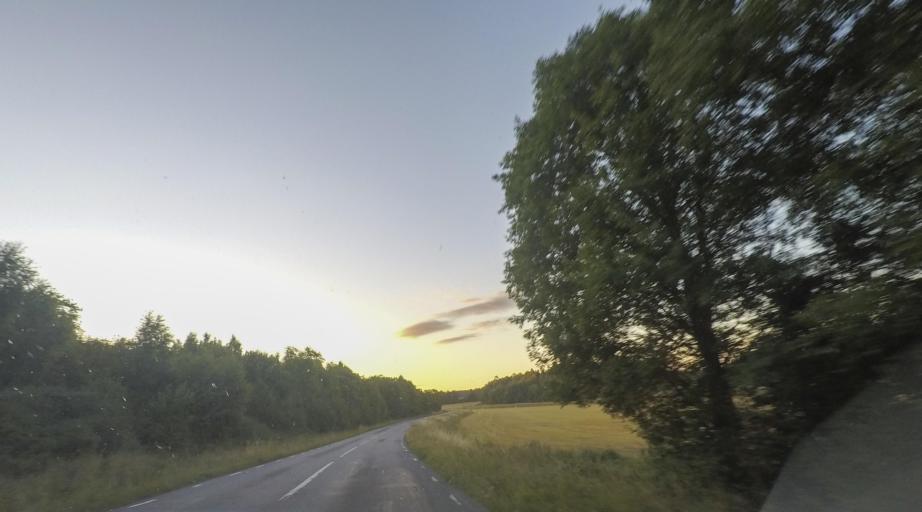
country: SE
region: Soedermanland
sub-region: Trosa Kommun
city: Trosa
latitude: 58.9814
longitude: 17.6865
